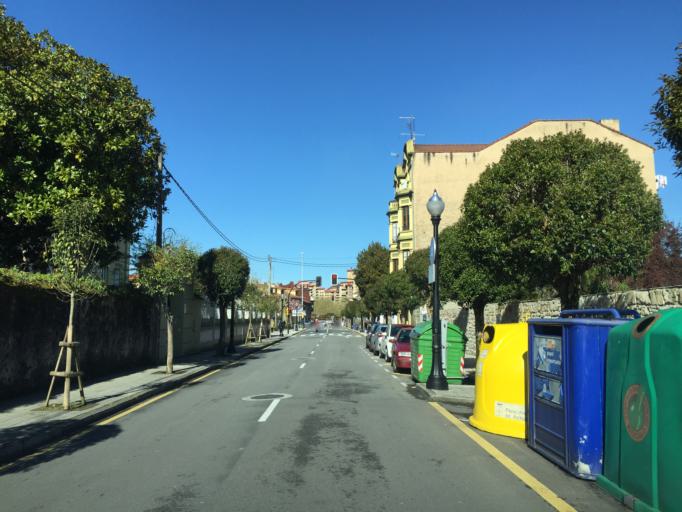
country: ES
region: Asturias
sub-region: Province of Asturias
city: Gijon
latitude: 43.5334
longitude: -5.6322
